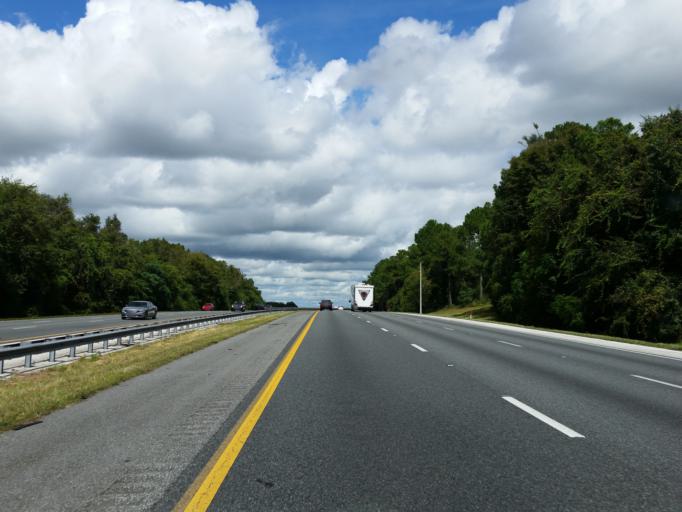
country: US
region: Florida
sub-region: Marion County
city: Ocala
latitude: 29.1165
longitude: -82.1848
